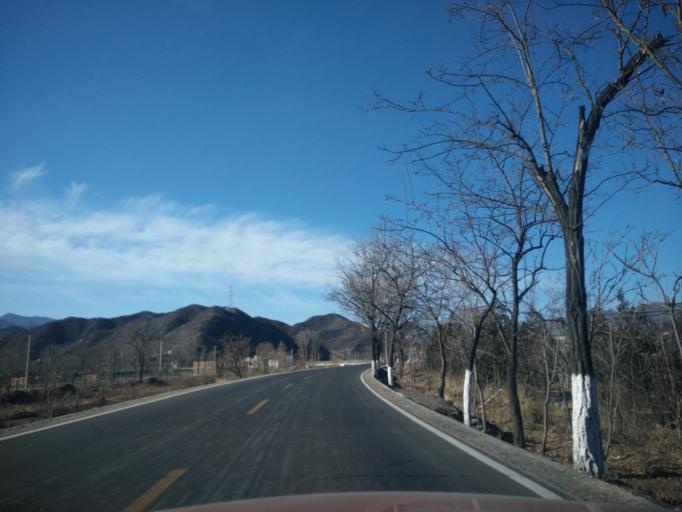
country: CN
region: Beijing
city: Zhaitang
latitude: 39.9803
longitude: 115.7194
